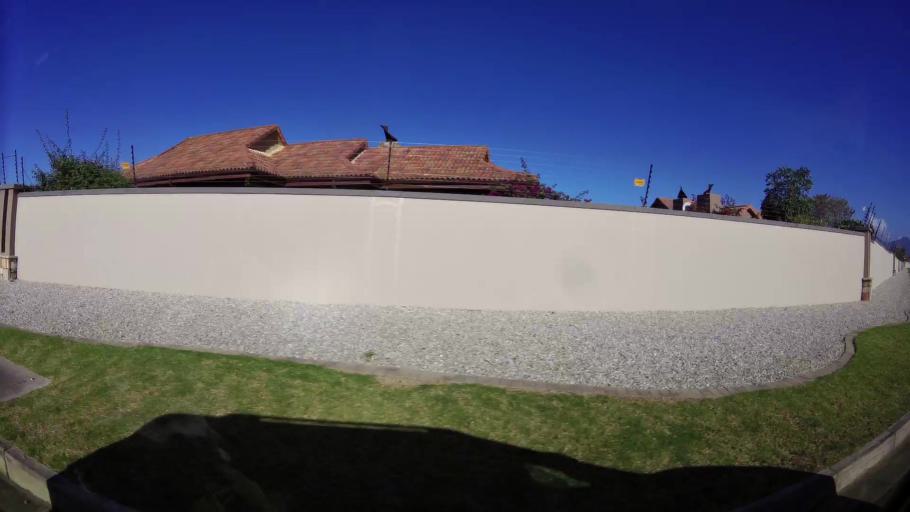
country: ZA
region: Western Cape
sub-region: Eden District Municipality
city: George
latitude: -33.9625
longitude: 22.4289
